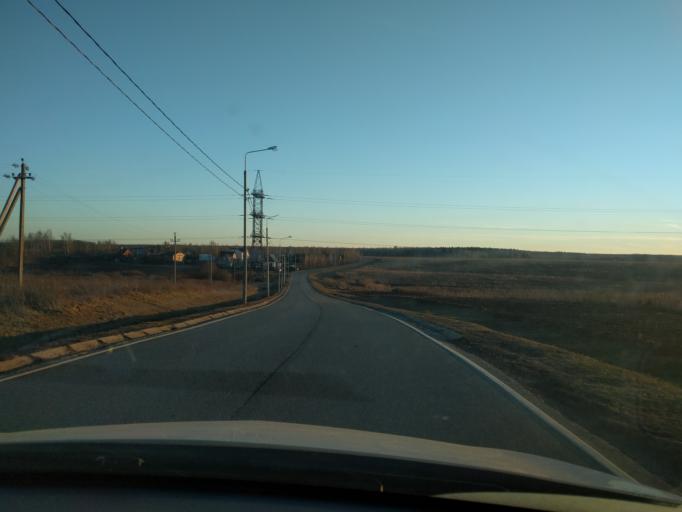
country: RU
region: Moskovskaya
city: Dubrovitsy
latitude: 55.4797
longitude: 37.4711
